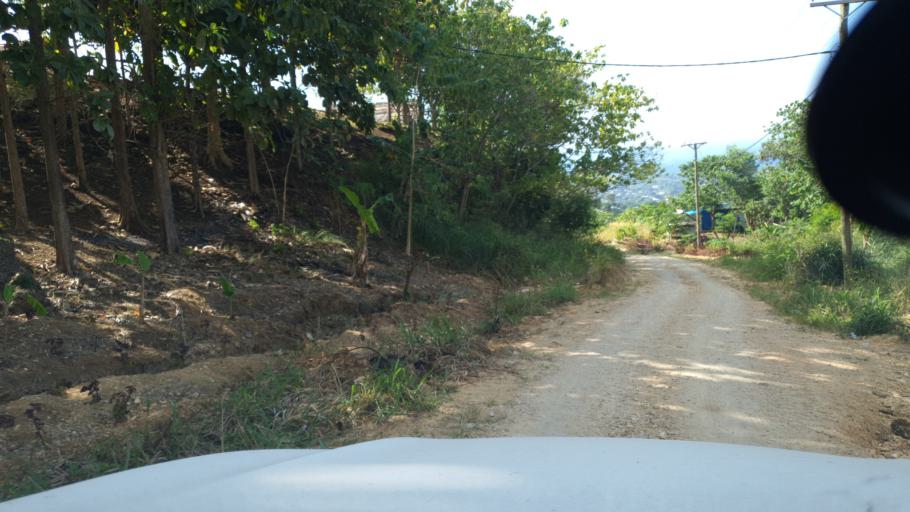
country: SB
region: Guadalcanal
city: Honiara
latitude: -9.4632
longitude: 159.9753
